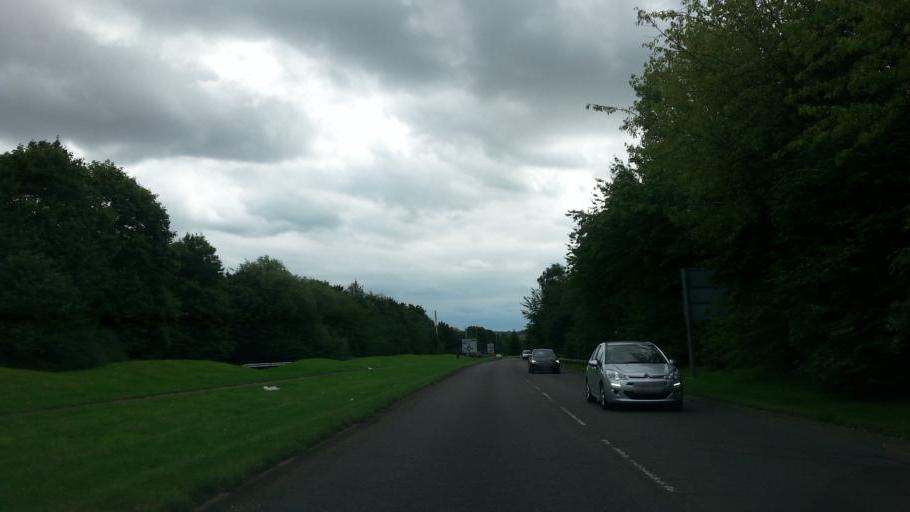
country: GB
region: England
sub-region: Northamptonshire
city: Earls Barton
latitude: 52.2602
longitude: -0.8102
